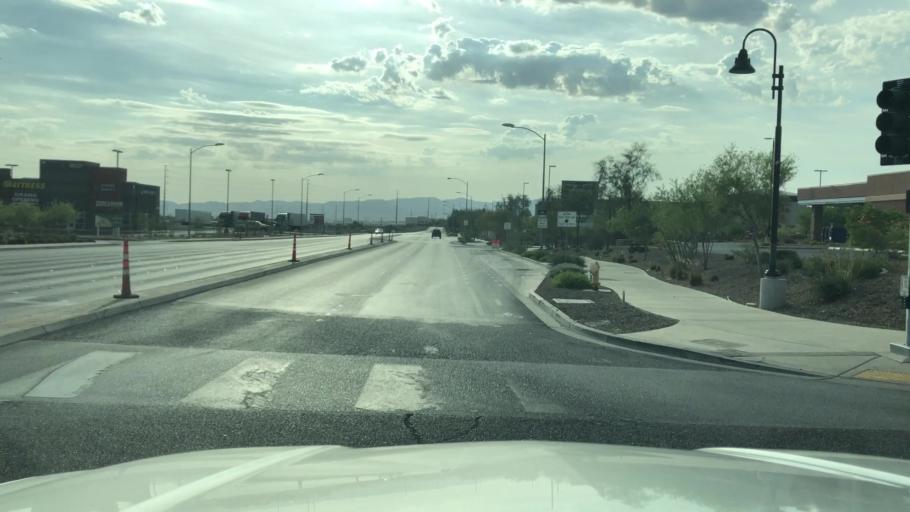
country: US
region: Nevada
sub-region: Clark County
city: Whitney
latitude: 36.0344
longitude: -115.0468
